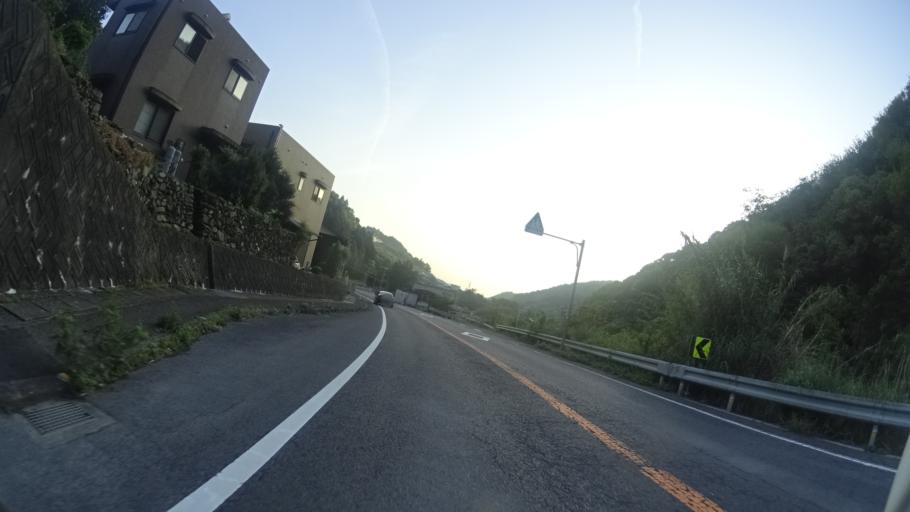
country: JP
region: Ehime
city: Kawanoecho
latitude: 33.9969
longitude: 133.6590
